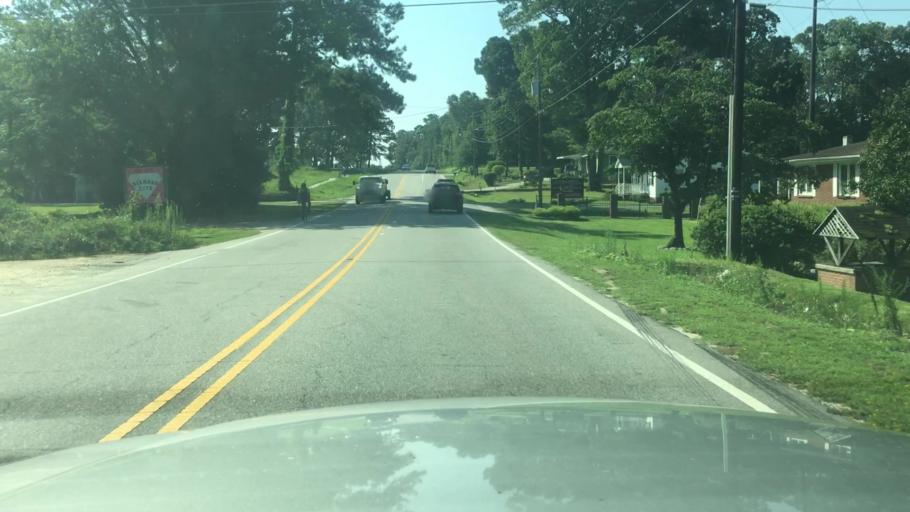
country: US
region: North Carolina
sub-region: Cumberland County
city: Fayetteville
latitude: 35.1214
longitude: -78.8854
